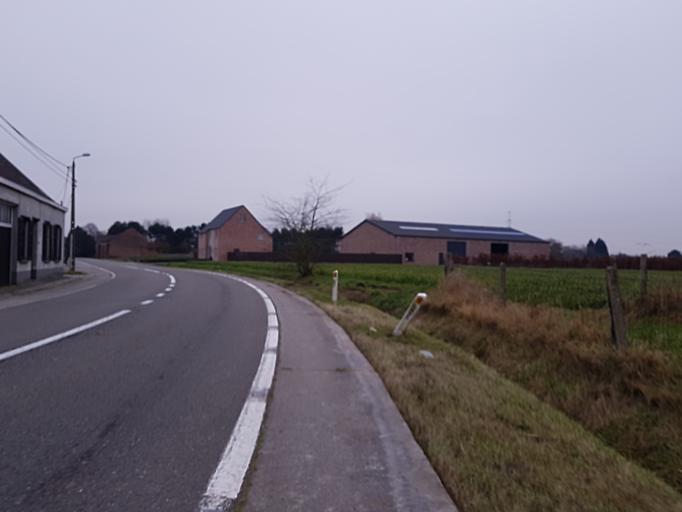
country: BE
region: Flanders
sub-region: Provincie Vlaams-Brabant
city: Kapelle-op-den-Bos
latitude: 51.0346
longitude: 4.3920
